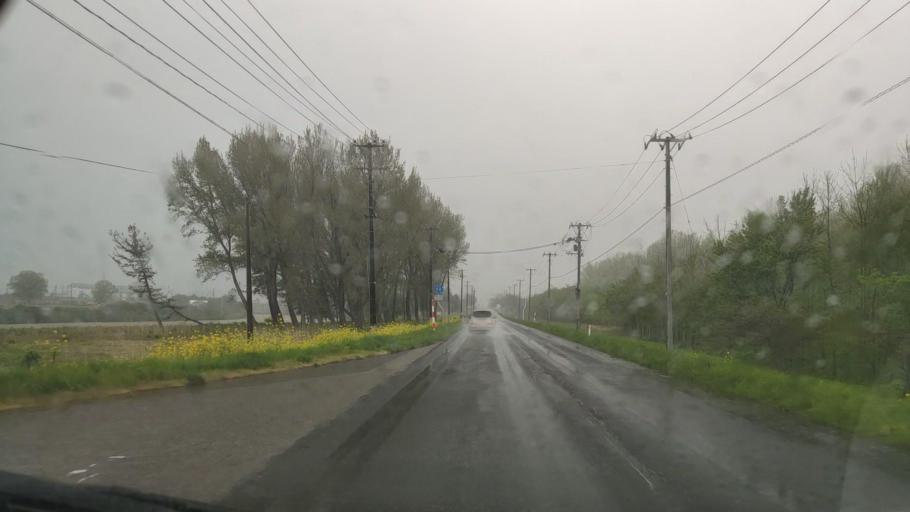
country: JP
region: Akita
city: Tenno
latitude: 39.9490
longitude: 139.9458
